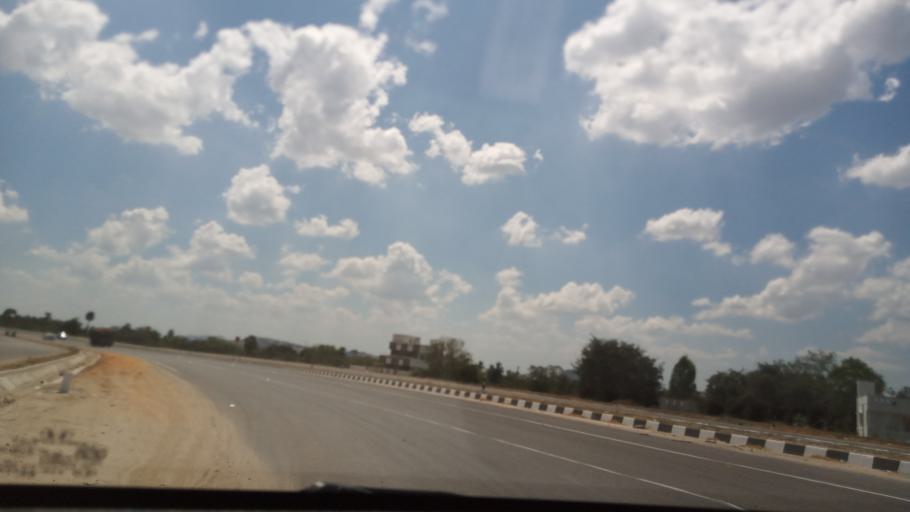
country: IN
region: Andhra Pradesh
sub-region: Chittoor
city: Pakala
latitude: 13.3342
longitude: 79.0770
